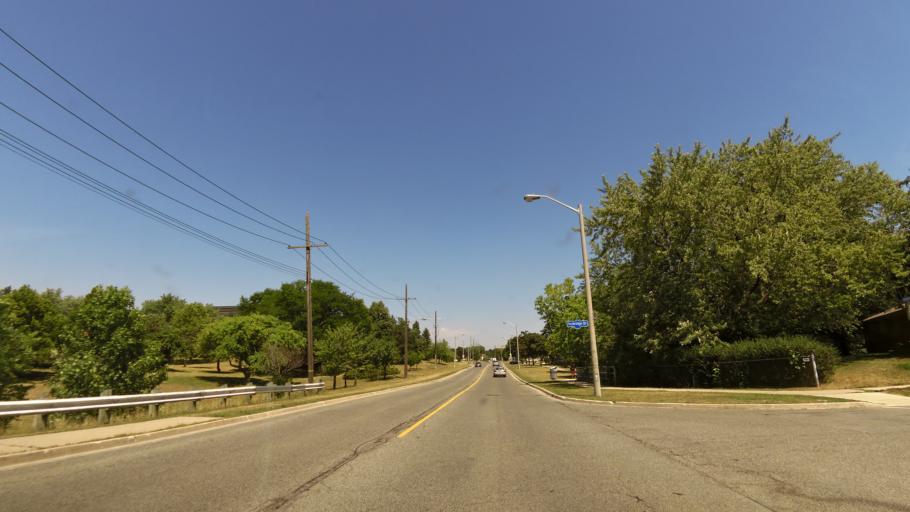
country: CA
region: Ontario
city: Etobicoke
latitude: 43.6484
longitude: -79.5853
